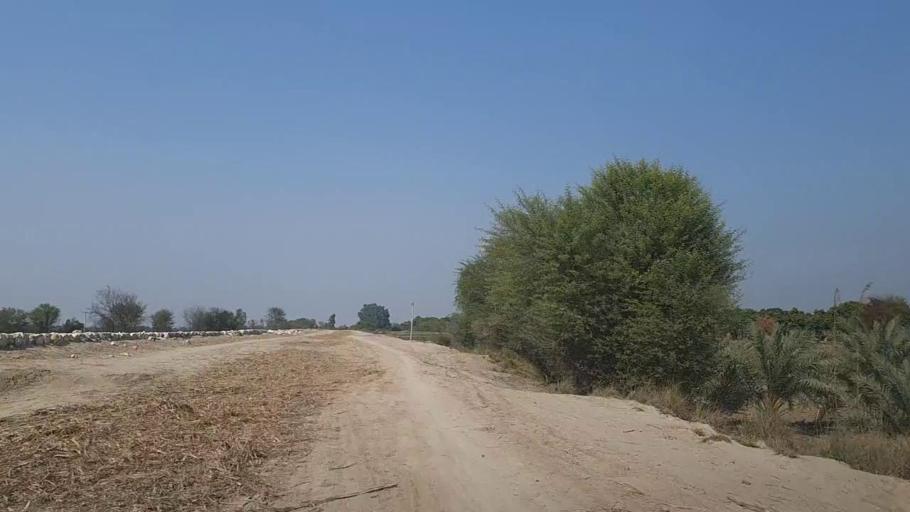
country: PK
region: Sindh
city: Moro
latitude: 26.8169
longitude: 67.9543
